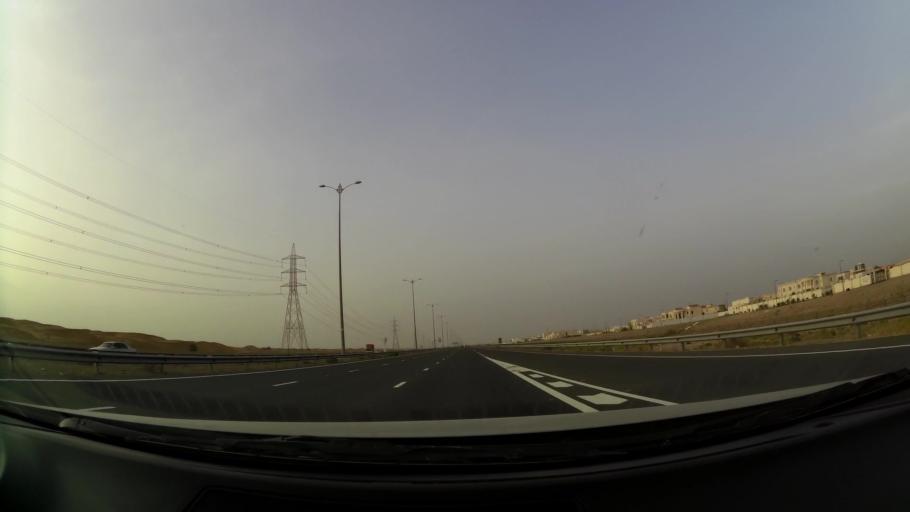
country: OM
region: Al Buraimi
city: Al Buraymi
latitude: 24.3504
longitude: 55.7807
